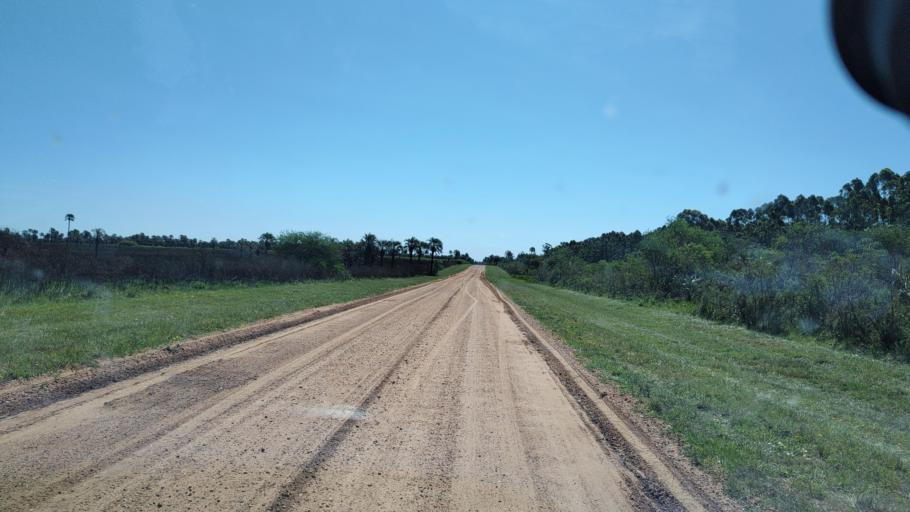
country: AR
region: Entre Rios
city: Ubajay
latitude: -31.8572
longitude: -58.2831
